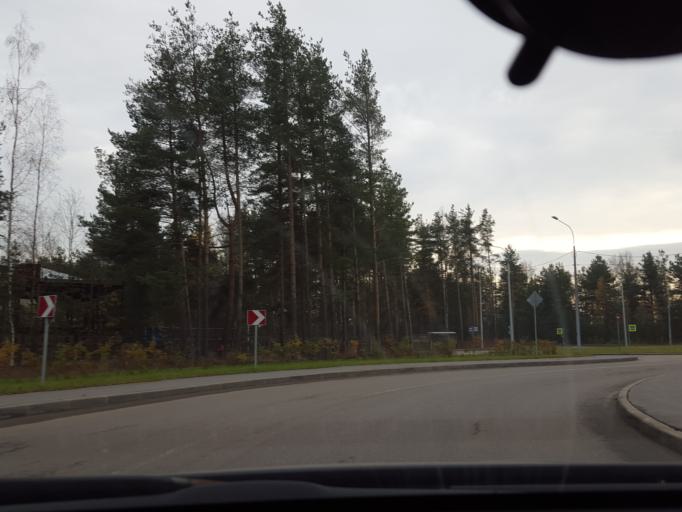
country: RU
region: St.-Petersburg
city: Kolomyagi
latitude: 60.0471
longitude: 30.2457
